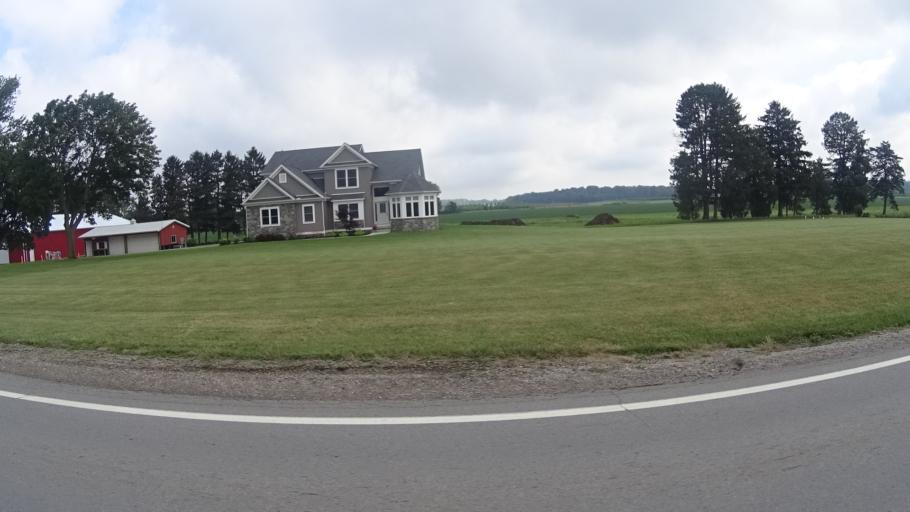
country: US
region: Ohio
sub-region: Huron County
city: Wakeman
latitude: 41.3061
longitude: -82.4705
